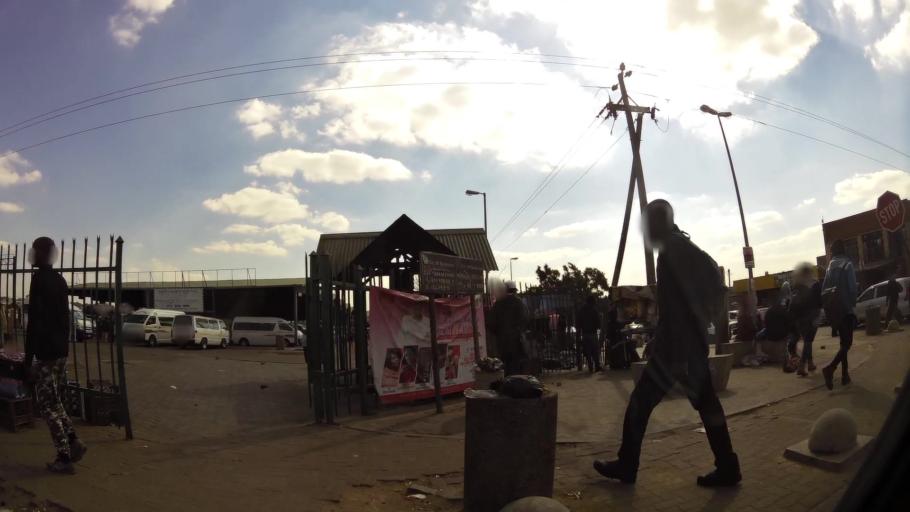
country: ZA
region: Gauteng
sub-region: Ekurhuleni Metropolitan Municipality
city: Tembisa
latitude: -26.0073
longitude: 28.1825
